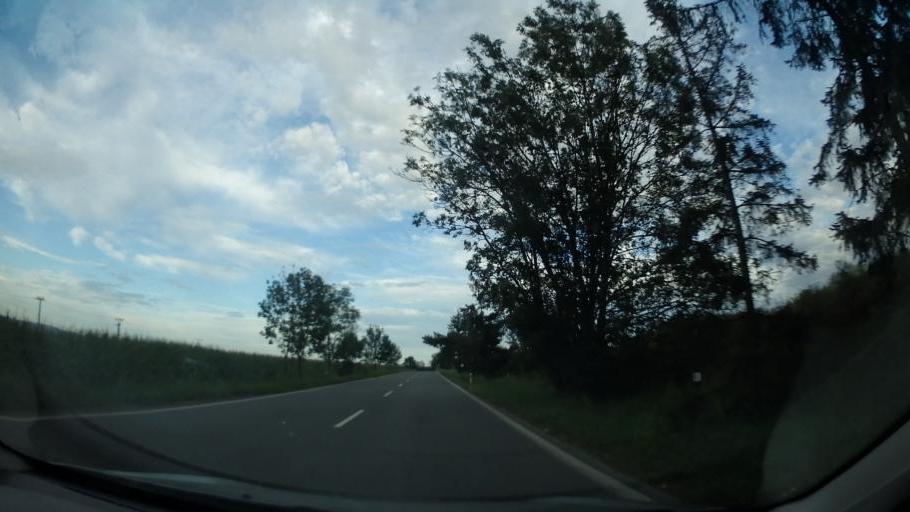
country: CZ
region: Olomoucky
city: Bila Lhota
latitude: 49.7030
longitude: 17.0051
